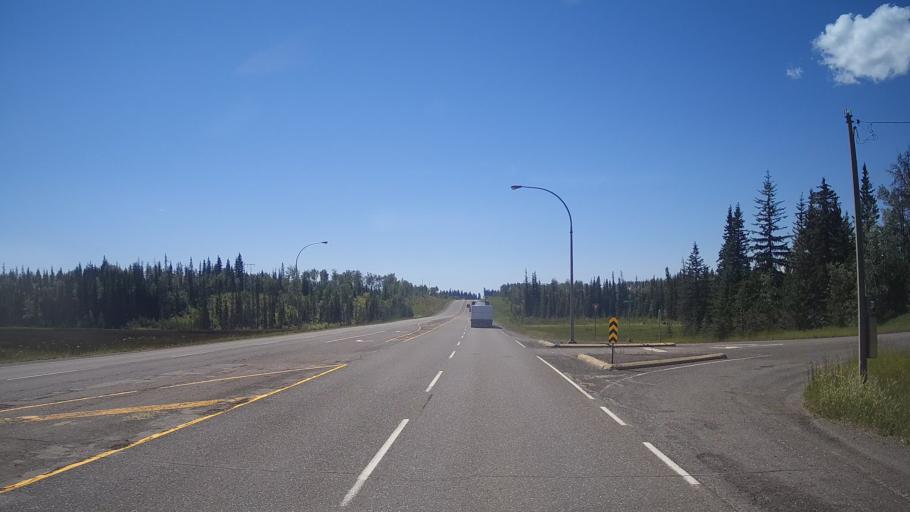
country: CA
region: British Columbia
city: Cache Creek
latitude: 51.4536
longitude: -121.3710
